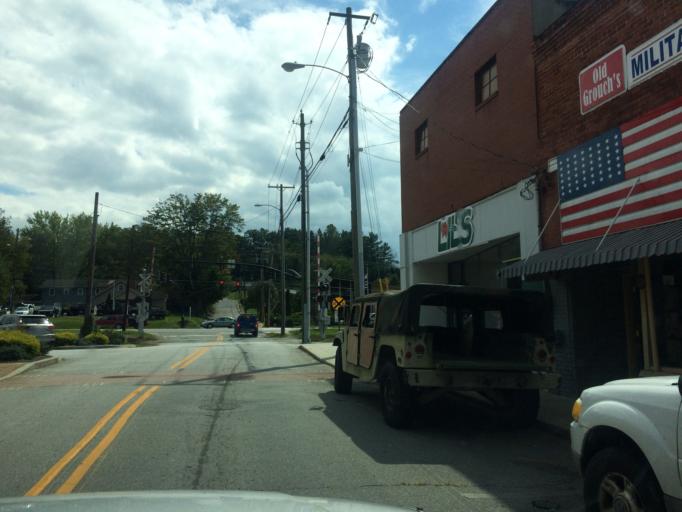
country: US
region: North Carolina
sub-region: Haywood County
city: Clyde
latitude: 35.5335
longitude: -82.9111
